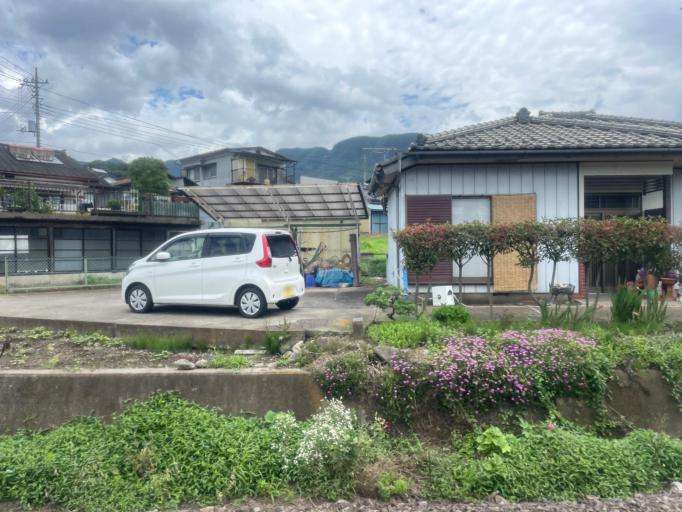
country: JP
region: Gunma
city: Numata
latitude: 36.6812
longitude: 138.9980
